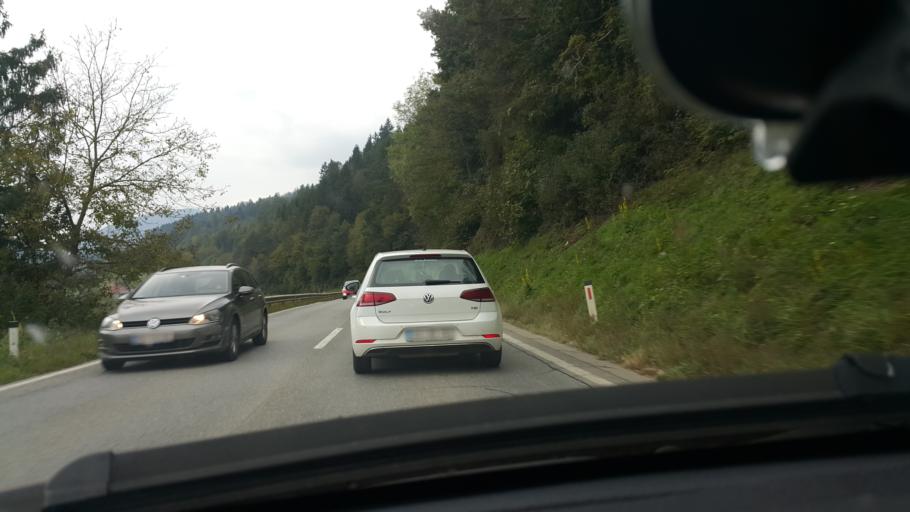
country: SI
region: Muta
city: Muta
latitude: 46.6165
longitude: 15.1856
